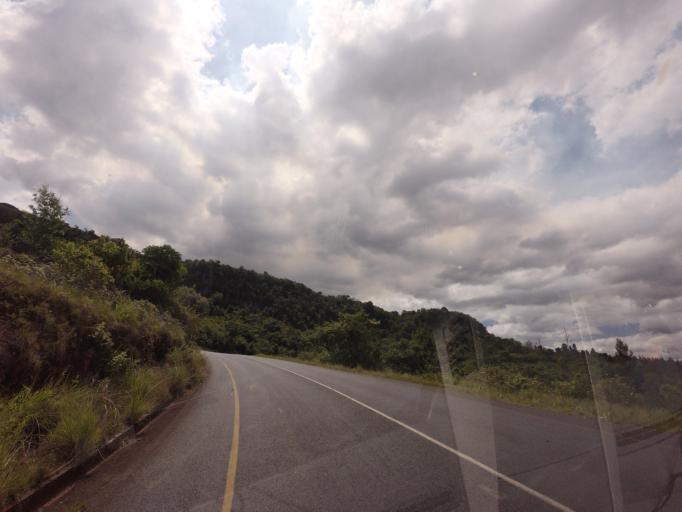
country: ZA
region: Mpumalanga
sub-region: Ehlanzeni District
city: Graksop
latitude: -24.9400
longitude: 30.8125
